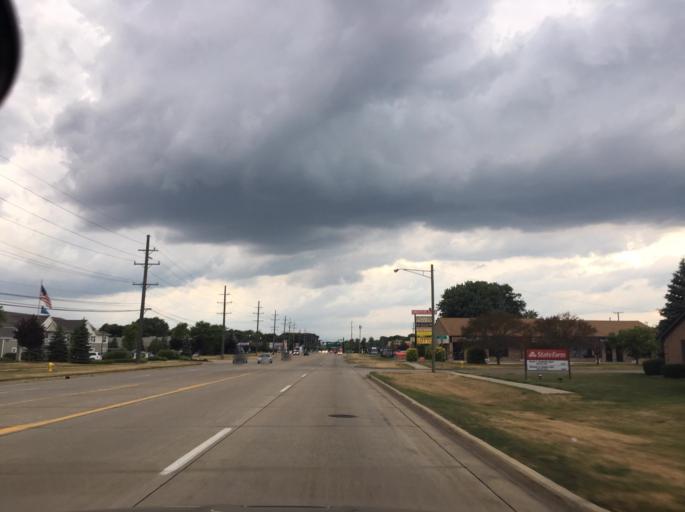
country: US
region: Michigan
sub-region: Macomb County
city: Fraser
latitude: 42.5623
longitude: -82.9506
